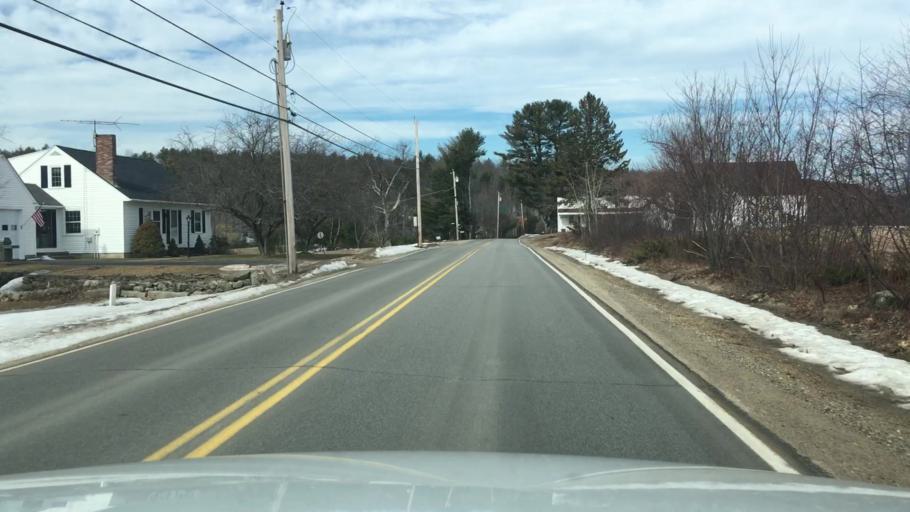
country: US
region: Maine
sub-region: York County
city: Springvale
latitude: 43.4971
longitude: -70.8125
